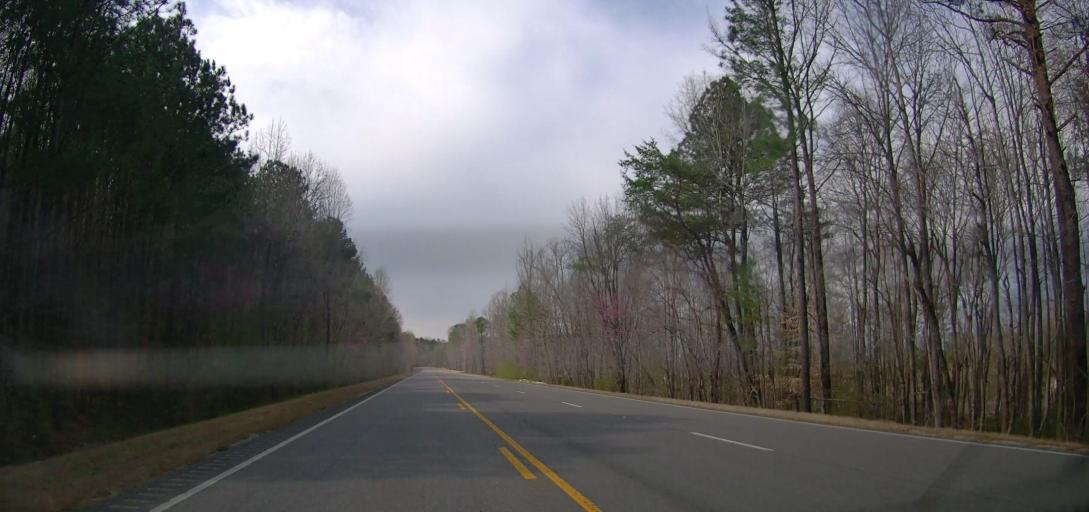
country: US
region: Alabama
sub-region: Walker County
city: Carbon Hill
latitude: 33.9127
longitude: -87.5619
